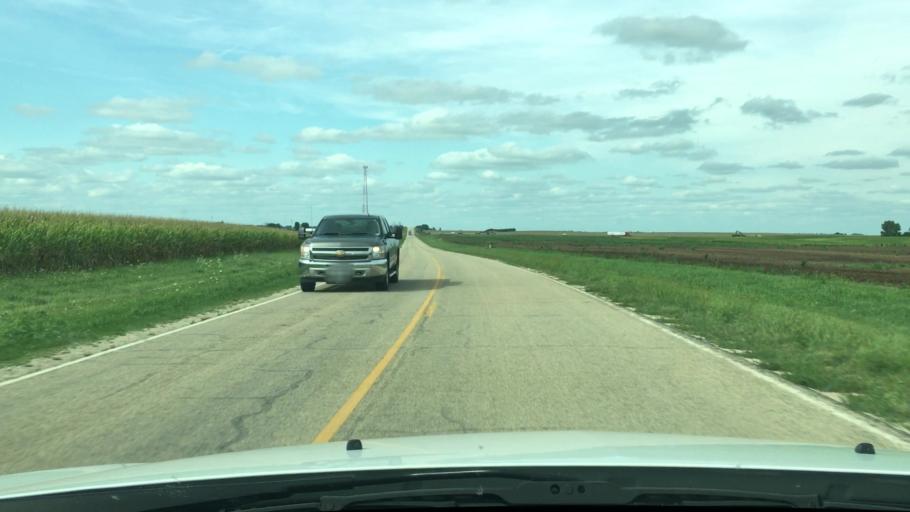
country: US
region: Illinois
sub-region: DeKalb County
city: Malta
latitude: 41.8931
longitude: -88.9608
